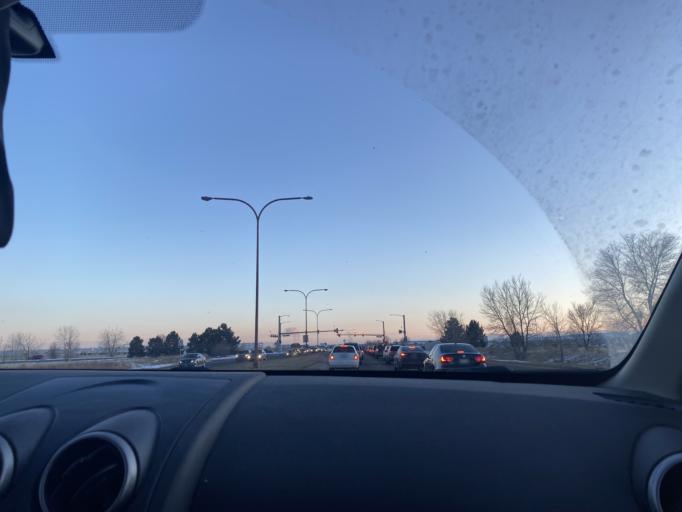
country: US
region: Colorado
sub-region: El Paso County
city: Cimarron Hills
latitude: 38.8080
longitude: -104.7303
